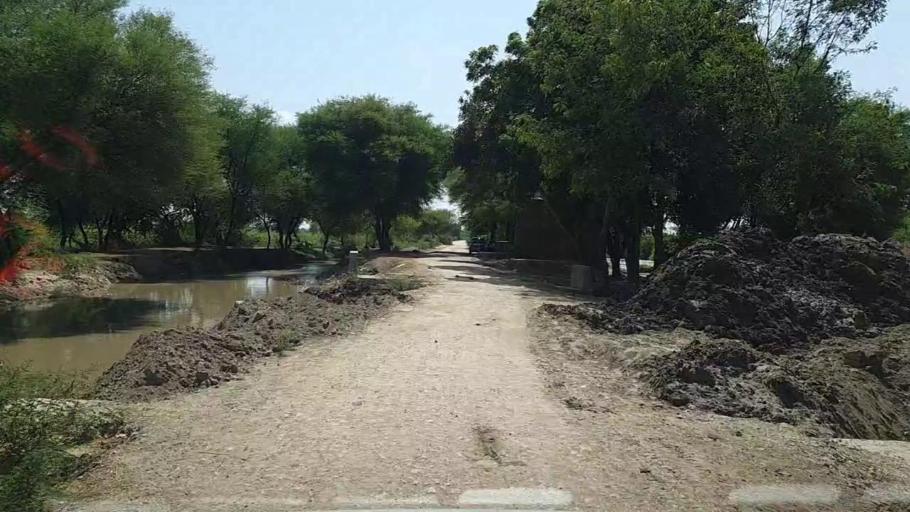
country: PK
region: Sindh
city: Kario
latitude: 24.8776
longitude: 68.6882
